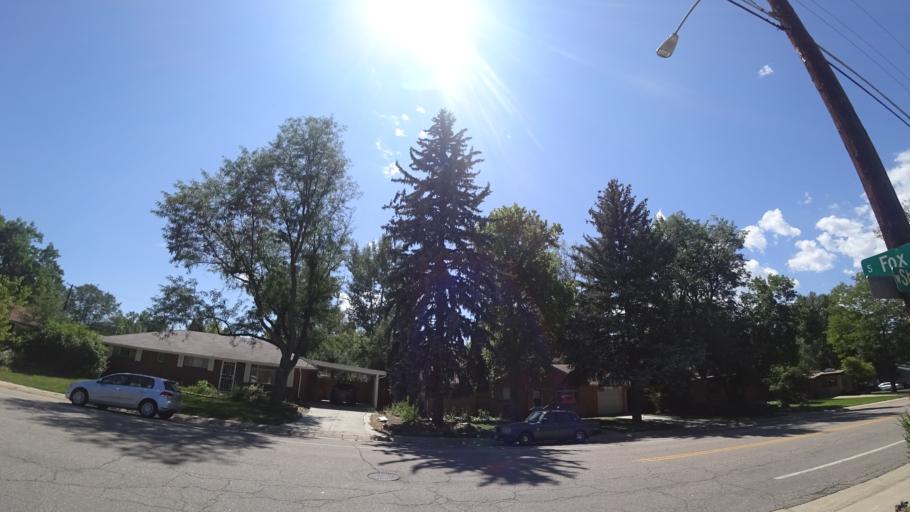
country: US
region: Colorado
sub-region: Arapahoe County
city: Littleton
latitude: 39.6101
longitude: -104.9965
